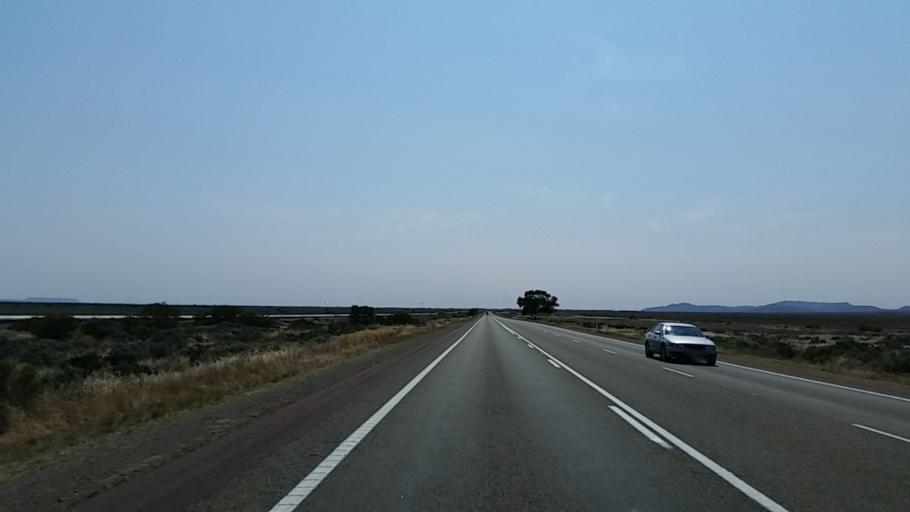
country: AU
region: South Australia
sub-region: Port Augusta
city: Port Augusta
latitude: -32.6758
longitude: 137.9354
